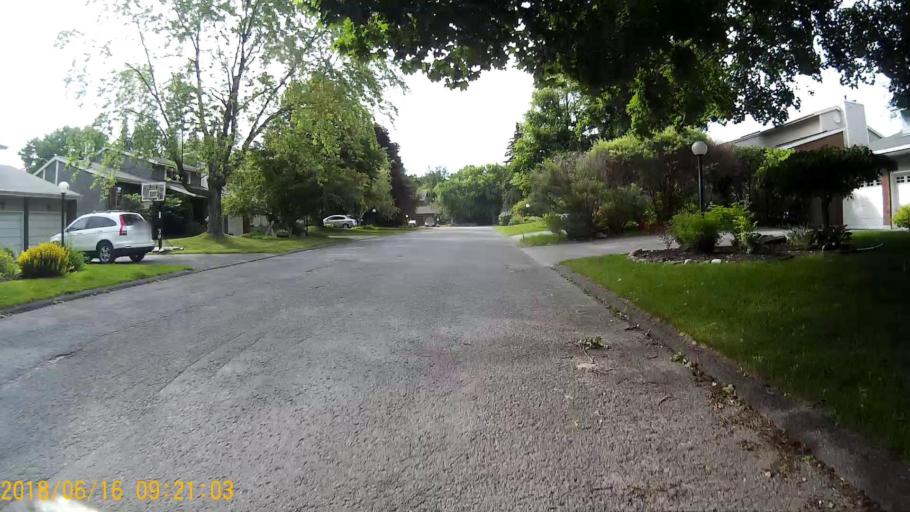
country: CA
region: Ontario
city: Bells Corners
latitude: 45.3119
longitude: -75.8924
